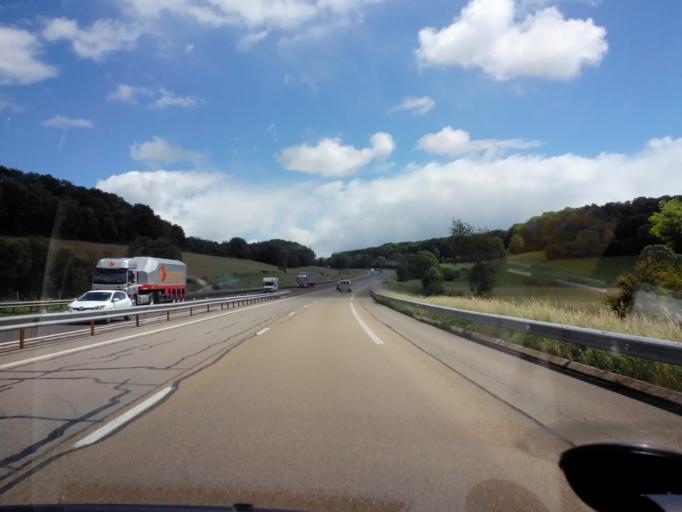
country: FR
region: Champagne-Ardenne
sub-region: Departement de la Haute-Marne
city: Avrecourt
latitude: 47.9593
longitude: 5.4520
